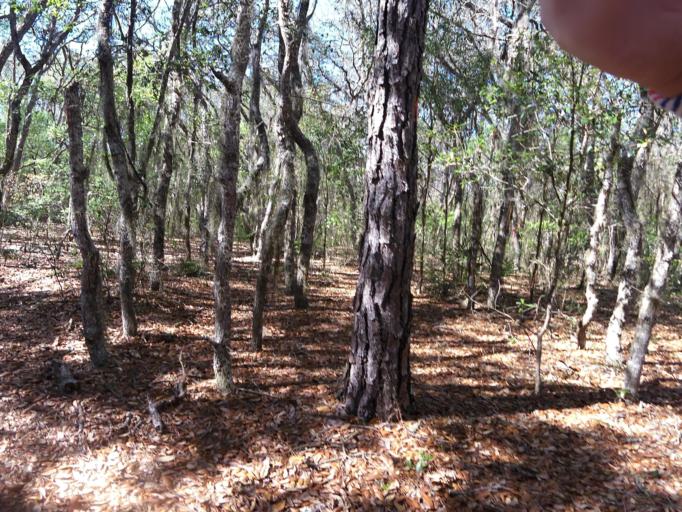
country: US
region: Florida
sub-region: Clay County
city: Keystone Heights
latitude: 29.8287
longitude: -82.0164
